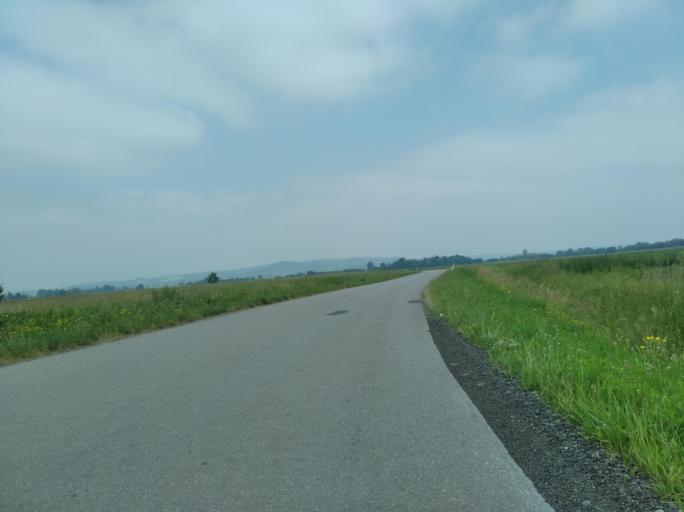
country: PL
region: Subcarpathian Voivodeship
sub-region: Powiat sanocki
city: Besko
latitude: 49.6092
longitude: 21.9550
